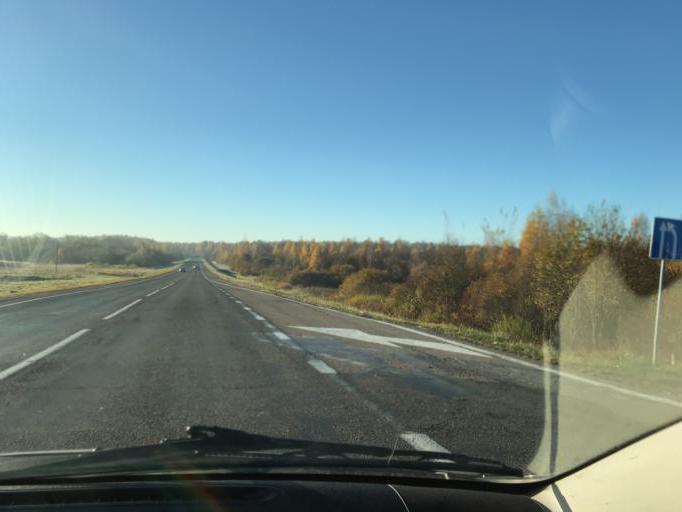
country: BY
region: Vitebsk
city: Vitebsk
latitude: 54.9074
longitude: 30.3761
